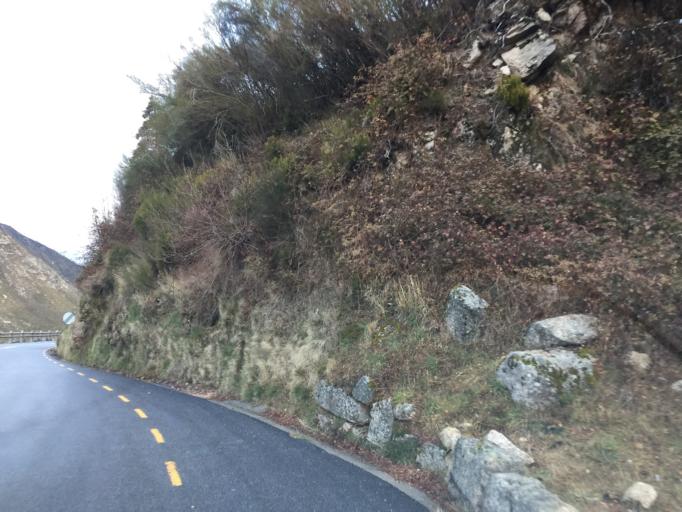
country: PT
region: Guarda
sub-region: Manteigas
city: Manteigas
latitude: 40.3442
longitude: -7.5627
